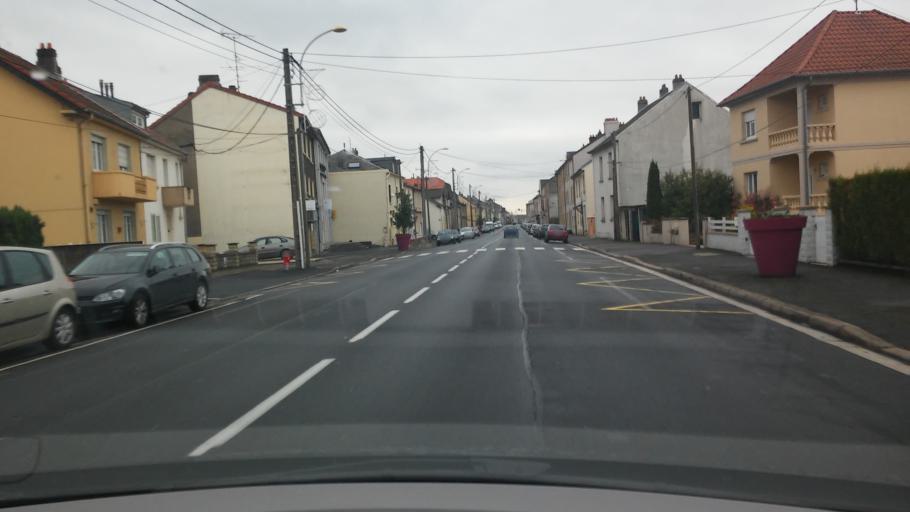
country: FR
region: Lorraine
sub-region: Departement de la Moselle
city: Hagondange
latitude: 49.2578
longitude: 6.1700
